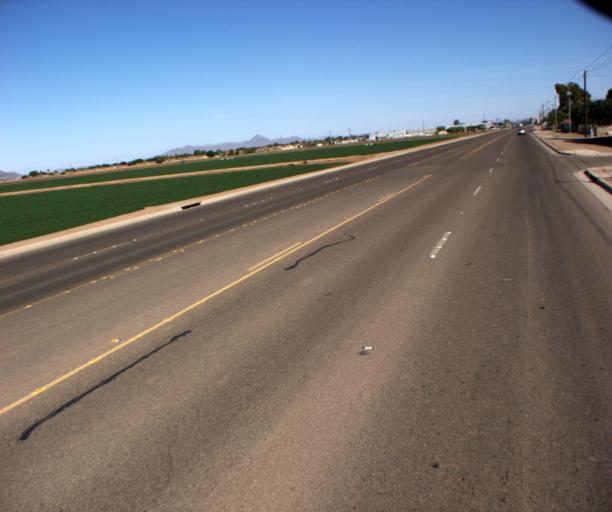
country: US
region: Arizona
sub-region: Yuma County
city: Yuma
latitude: 32.6629
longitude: -114.6501
